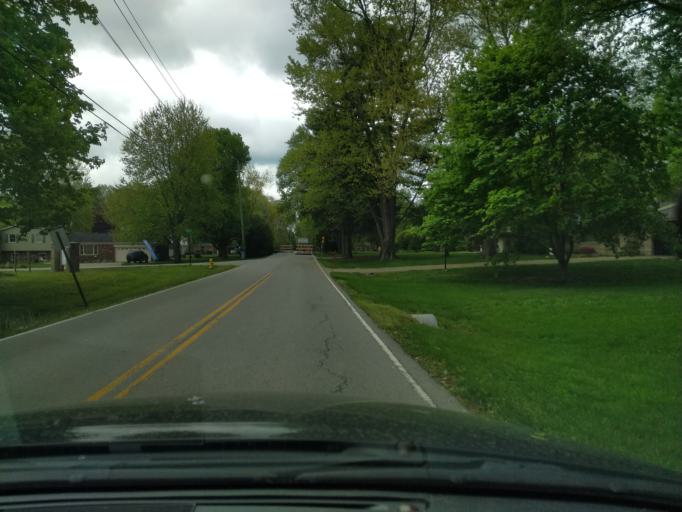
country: US
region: Indiana
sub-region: Hamilton County
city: Carmel
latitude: 39.9314
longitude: -86.1173
